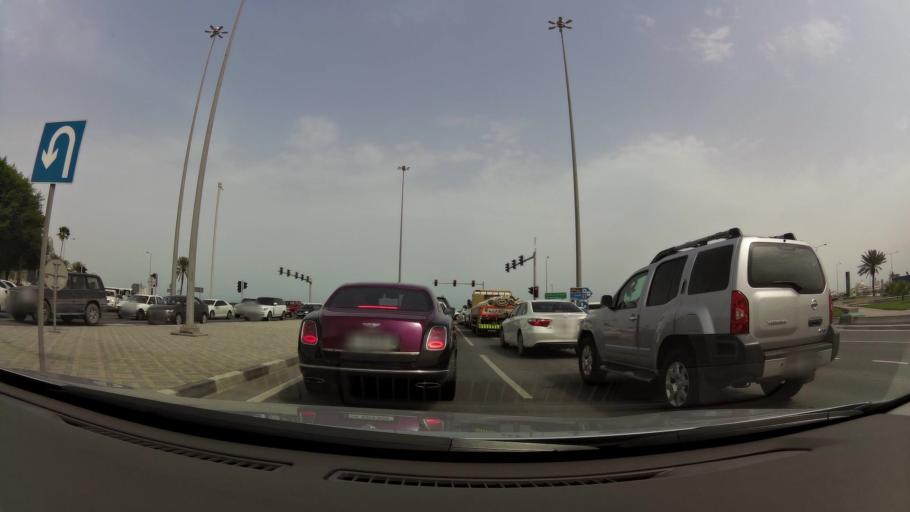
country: QA
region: Baladiyat ad Dawhah
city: Doha
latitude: 25.3042
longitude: 51.5172
